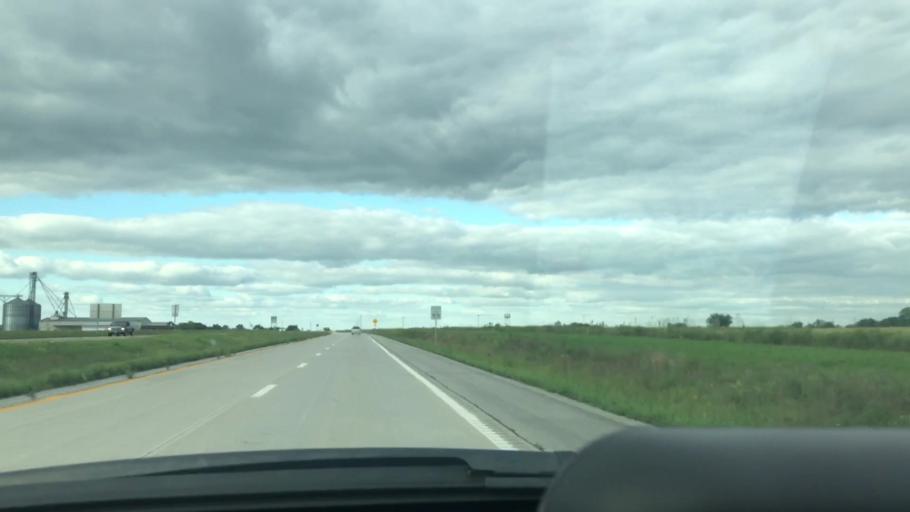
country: US
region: Missouri
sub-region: Benton County
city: Lincoln
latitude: 38.3778
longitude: -93.3368
